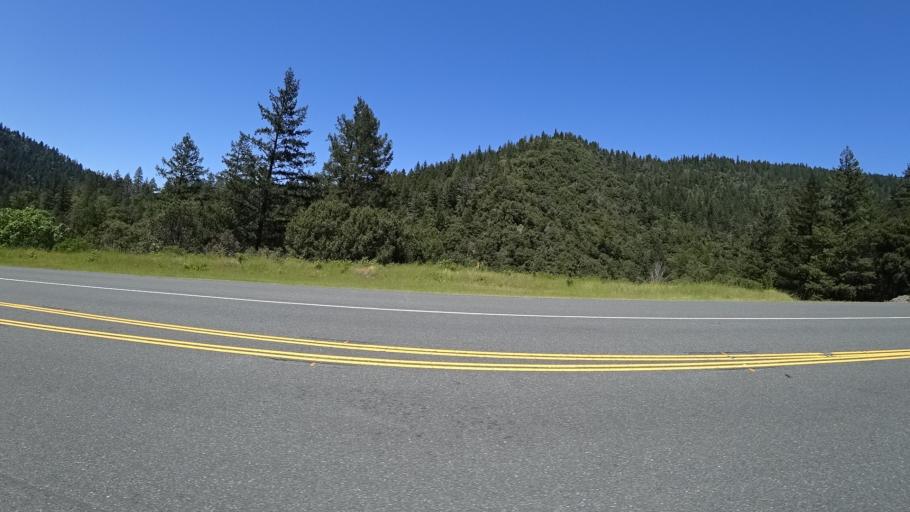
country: US
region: California
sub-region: Humboldt County
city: Willow Creek
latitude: 40.8834
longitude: -123.5474
